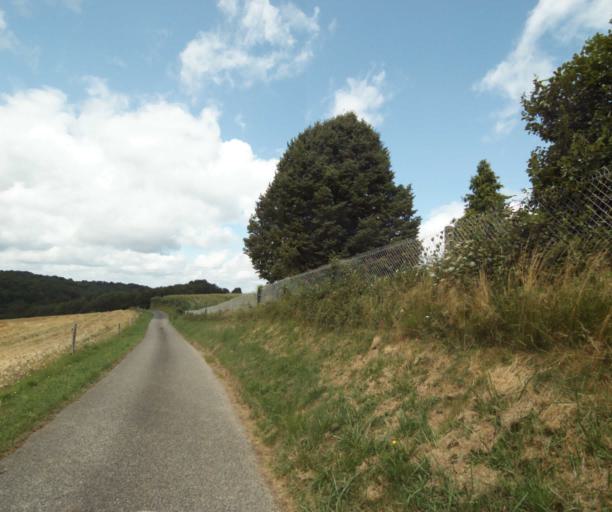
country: FR
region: Limousin
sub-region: Departement de la Correze
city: Sainte-Fortunade
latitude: 45.2112
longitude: 1.8091
